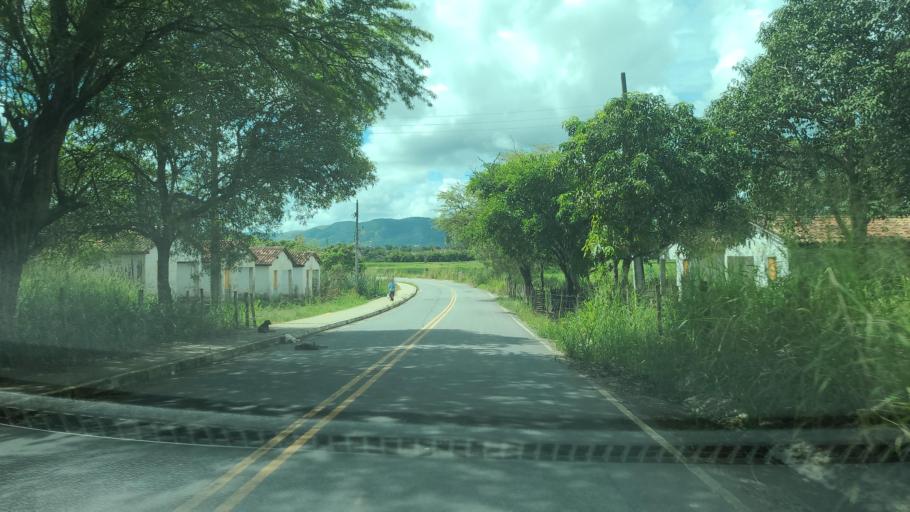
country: BR
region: Alagoas
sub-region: Uniao Dos Palmares
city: Uniao dos Palmares
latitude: -9.1628
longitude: -36.0496
